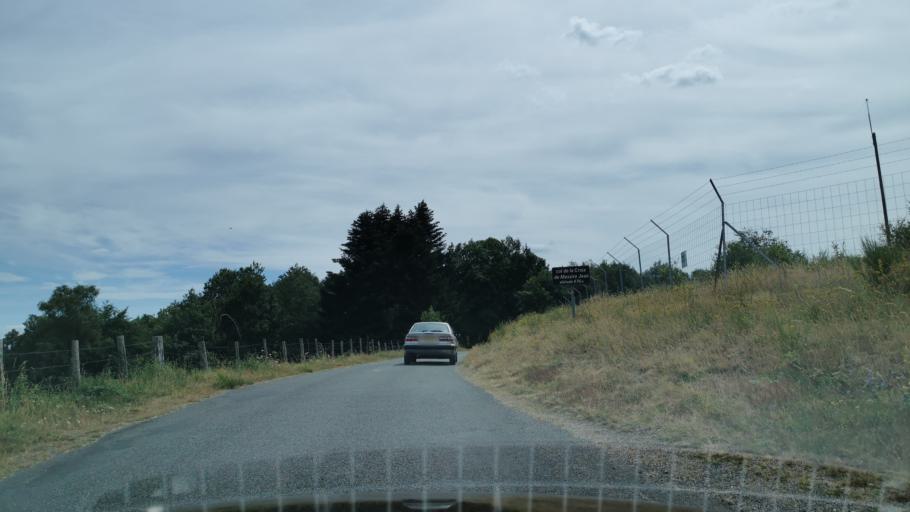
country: FR
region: Bourgogne
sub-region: Departement de Saone-et-Loire
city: Etang-sur-Arroux
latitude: 46.8062
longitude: 4.2600
